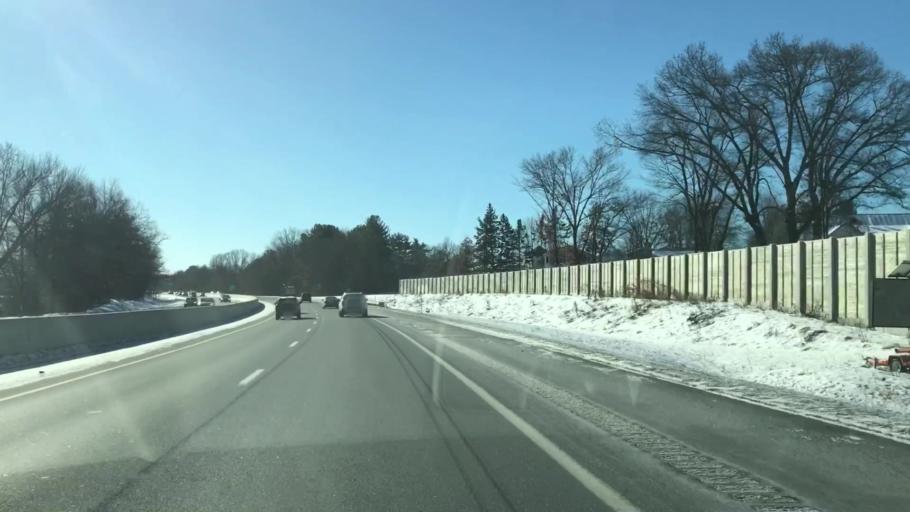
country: US
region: New Hampshire
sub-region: Hillsborough County
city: Manchester
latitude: 42.9678
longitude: -71.4770
